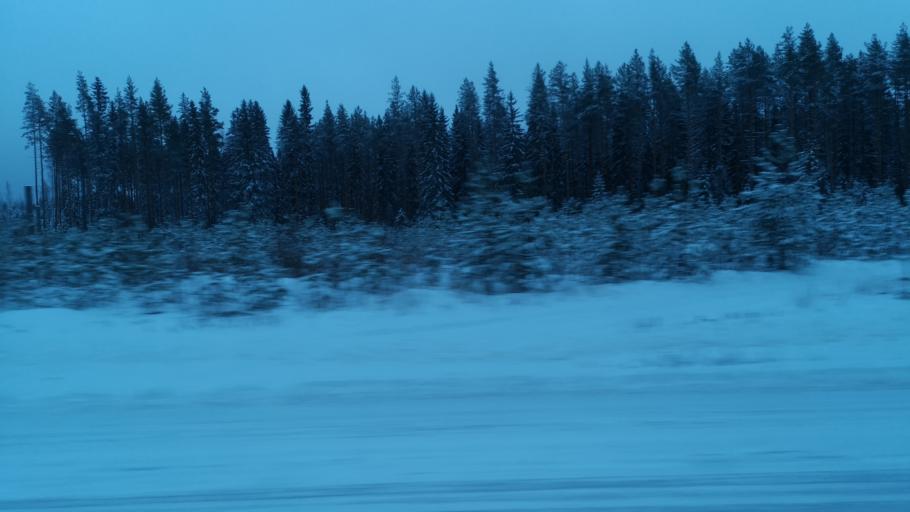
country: FI
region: Southern Savonia
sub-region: Savonlinna
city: Savonlinna
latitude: 61.9690
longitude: 28.8165
